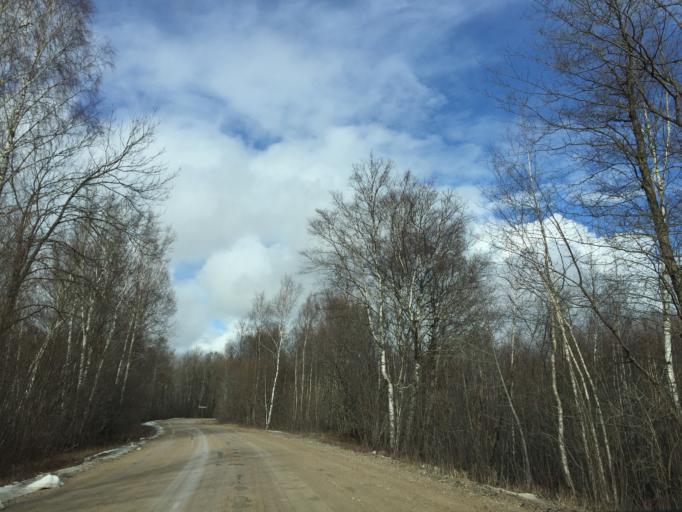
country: EE
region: Laeaene
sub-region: Lihula vald
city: Lihula
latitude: 58.7258
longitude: 23.8300
